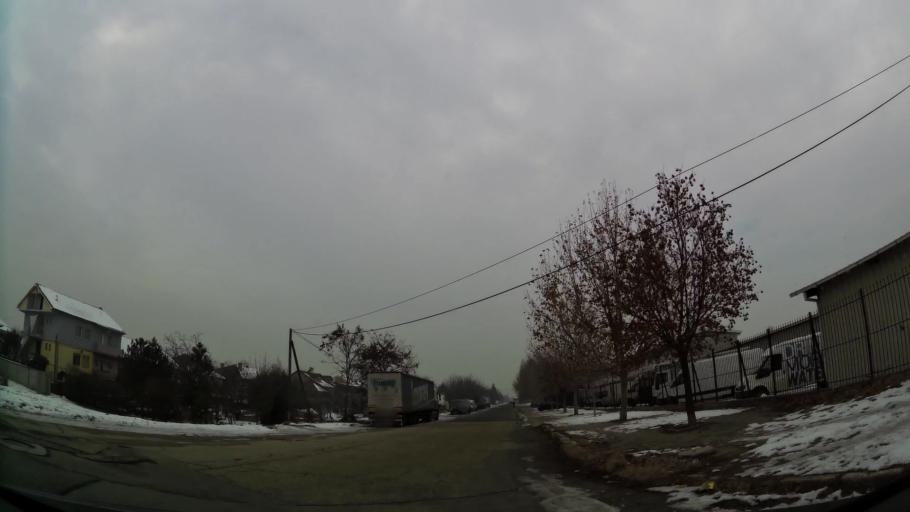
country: MK
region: Saraj
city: Saraj
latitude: 42.0179
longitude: 21.3625
